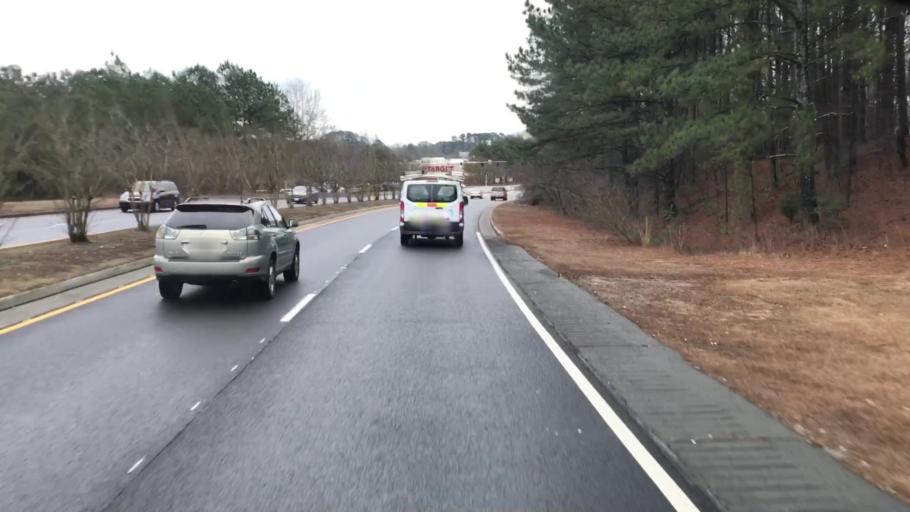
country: US
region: Georgia
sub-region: Gwinnett County
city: Snellville
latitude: 33.8748
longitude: -84.0201
